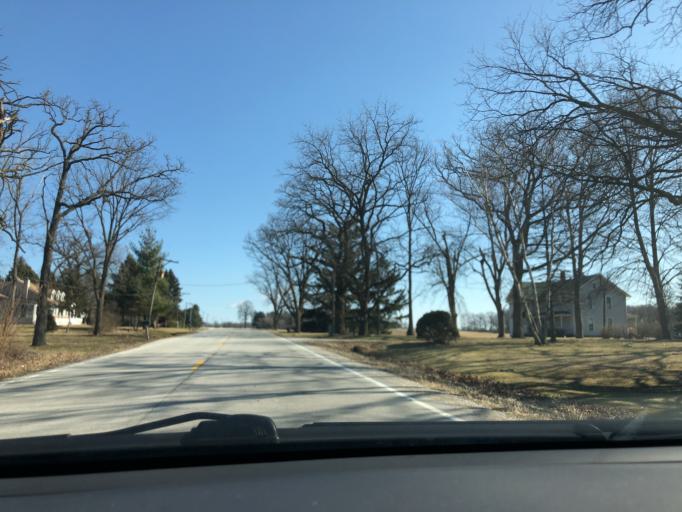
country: US
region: Illinois
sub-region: Kane County
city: Hampshire
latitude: 42.1062
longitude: -88.5029
